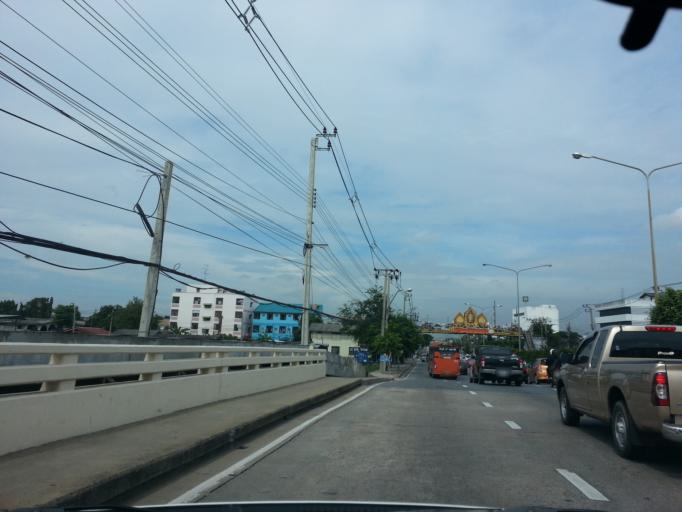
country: TH
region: Bangkok
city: Bueng Kum
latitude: 13.7933
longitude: 100.6862
